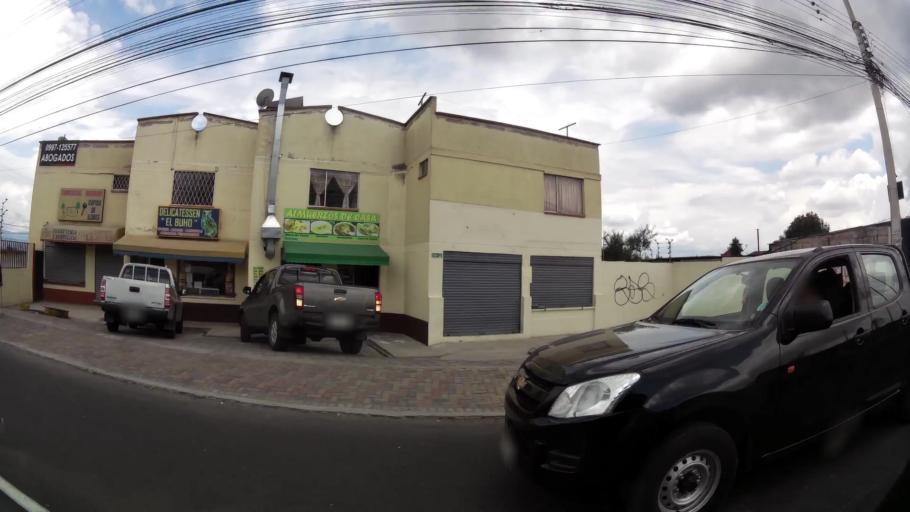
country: EC
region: Pichincha
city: Quito
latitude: -0.0935
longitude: -78.4358
